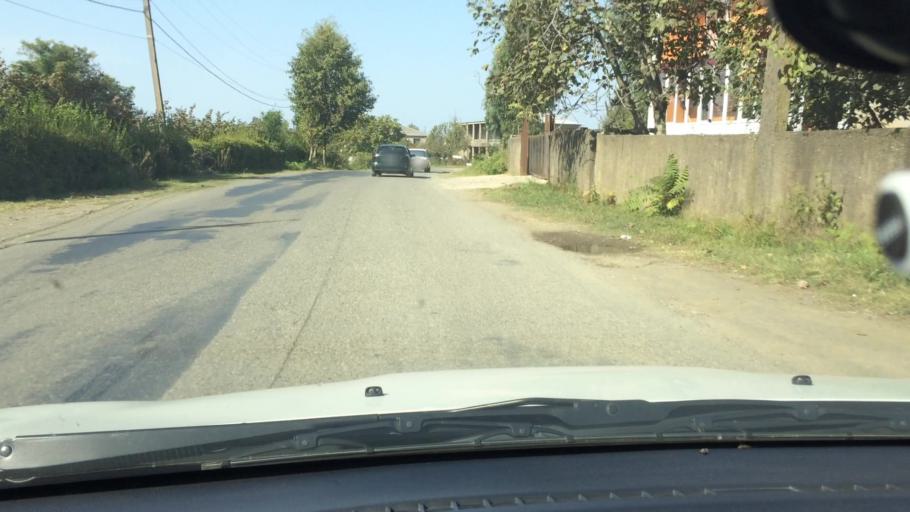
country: GE
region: Ajaria
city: Kobuleti
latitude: 41.8045
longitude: 41.8029
